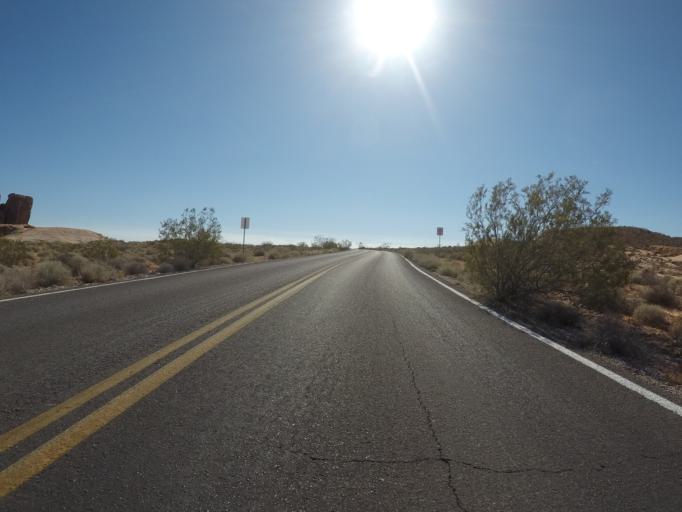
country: US
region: Nevada
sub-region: Clark County
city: Moapa Valley
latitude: 36.4898
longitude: -114.5294
